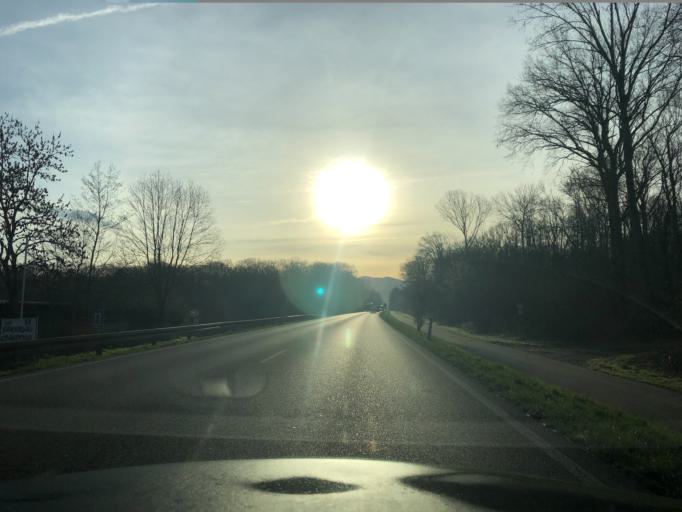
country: DE
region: Baden-Wuerttemberg
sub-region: Freiburg Region
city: Vorstetten
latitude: 48.0600
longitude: 7.8219
